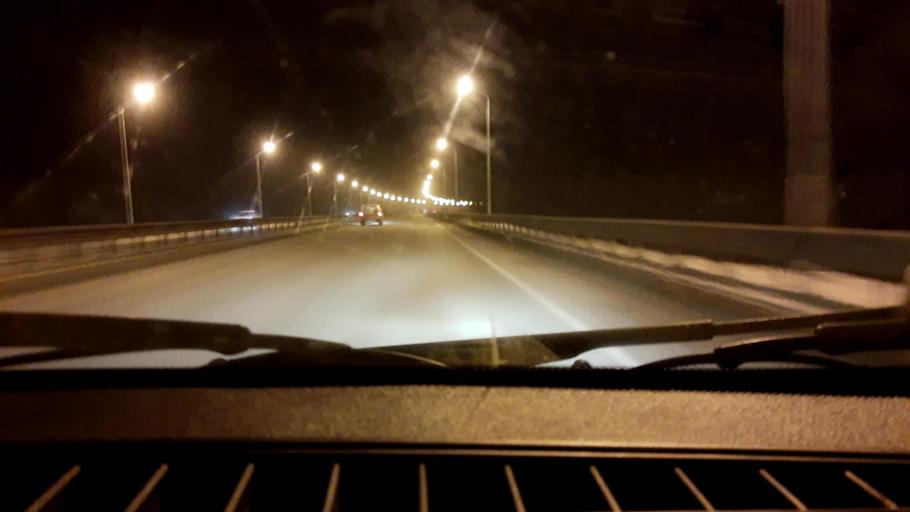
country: RU
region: Bashkortostan
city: Ufa
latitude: 54.6724
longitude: 56.0340
